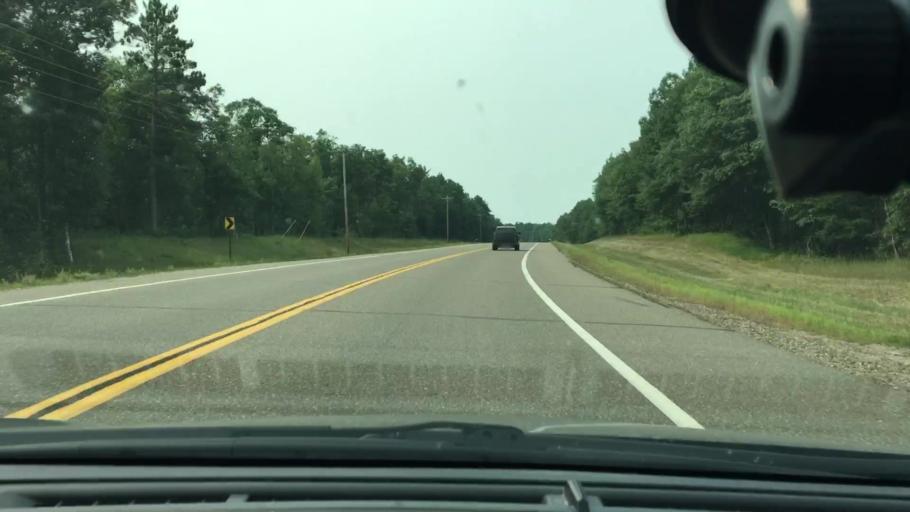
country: US
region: Minnesota
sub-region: Crow Wing County
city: Breezy Point
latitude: 46.5656
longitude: -94.1297
